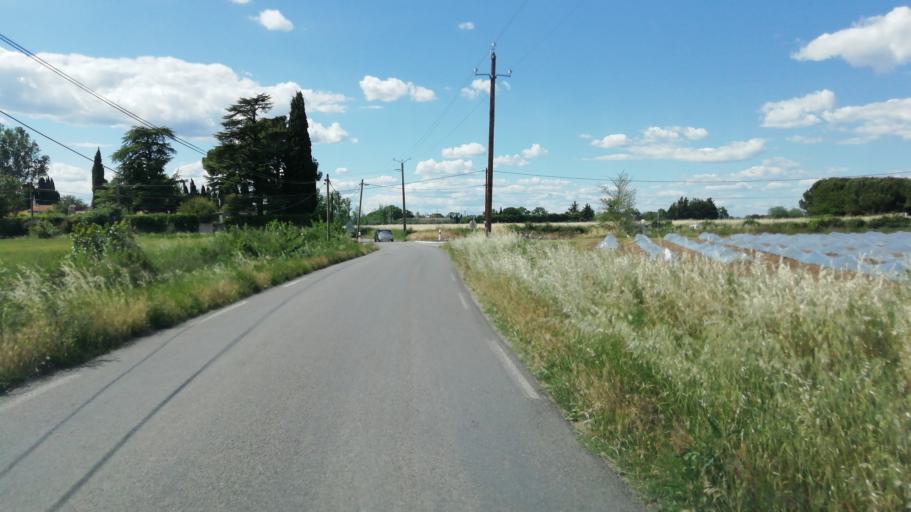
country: FR
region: Languedoc-Roussillon
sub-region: Departement de l'Herault
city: Saint-Just
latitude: 43.6639
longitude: 4.1082
